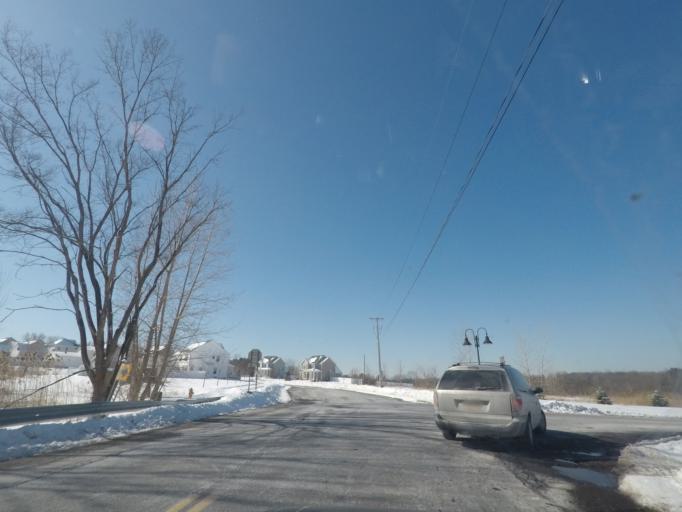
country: US
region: New York
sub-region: Saratoga County
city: Ballston Spa
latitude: 42.9924
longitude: -73.7986
